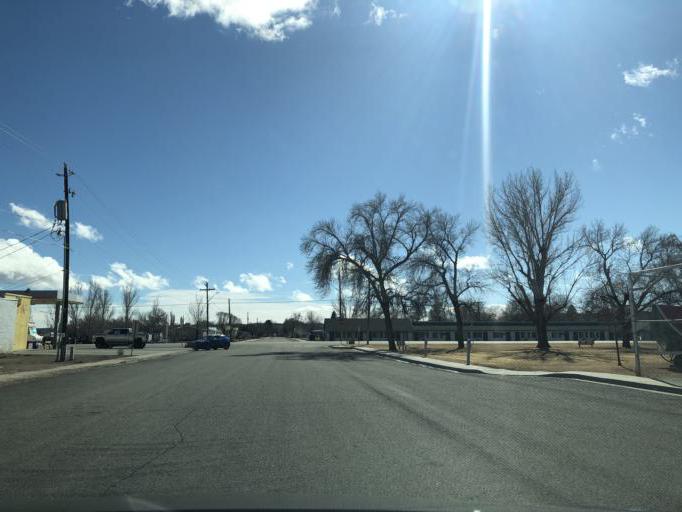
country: US
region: Utah
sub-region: Carbon County
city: East Carbon City
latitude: 38.9963
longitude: -110.1599
